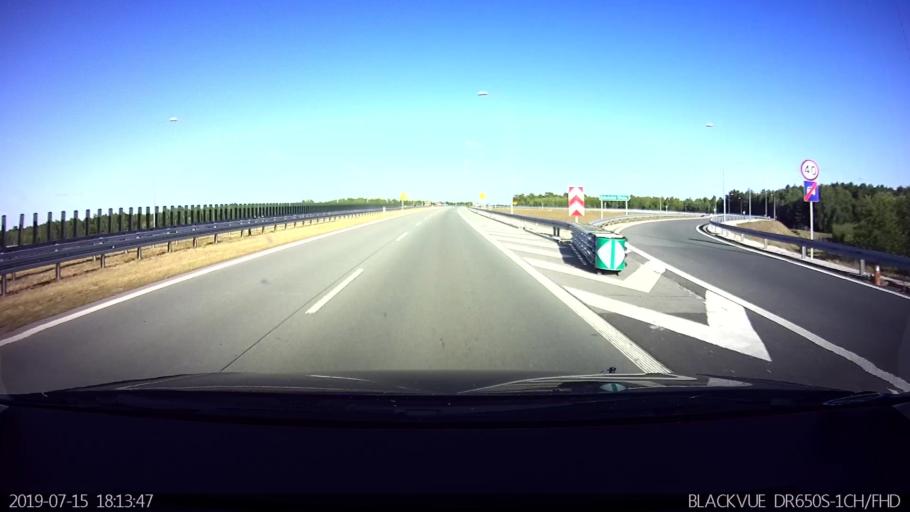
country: PL
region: Lodz Voivodeship
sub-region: Powiat zdunskowolski
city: Zapolice
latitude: 51.5977
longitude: 18.8716
